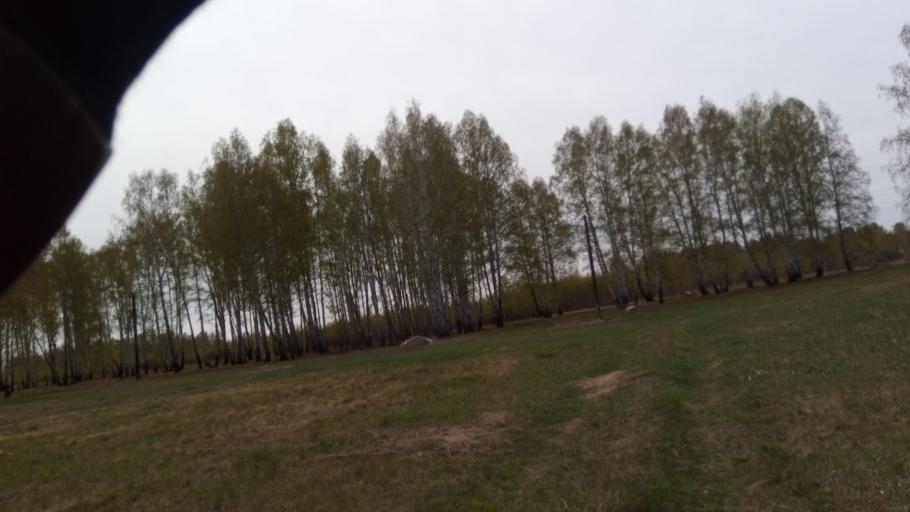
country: RU
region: Chelyabinsk
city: Timiryazevskiy
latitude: 54.9990
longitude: 60.8513
